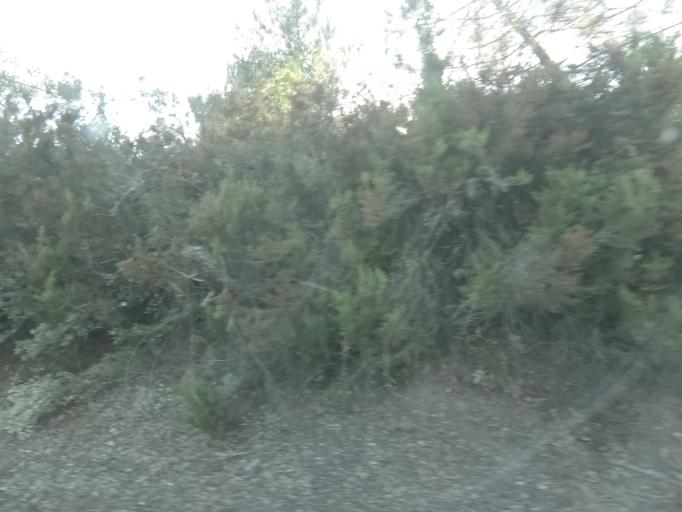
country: PT
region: Vila Real
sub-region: Sabrosa
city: Vilela
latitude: 41.1718
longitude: -7.5904
